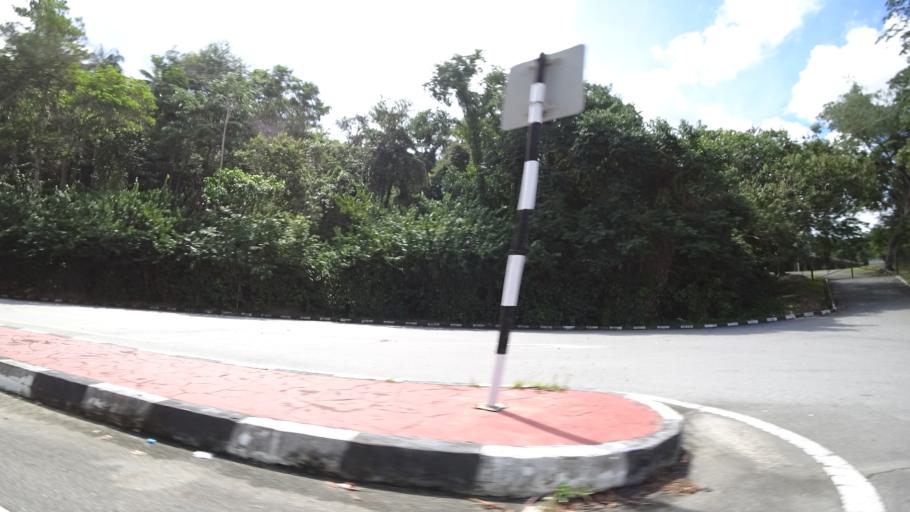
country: BN
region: Brunei and Muara
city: Bandar Seri Begawan
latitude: 4.8854
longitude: 114.9680
